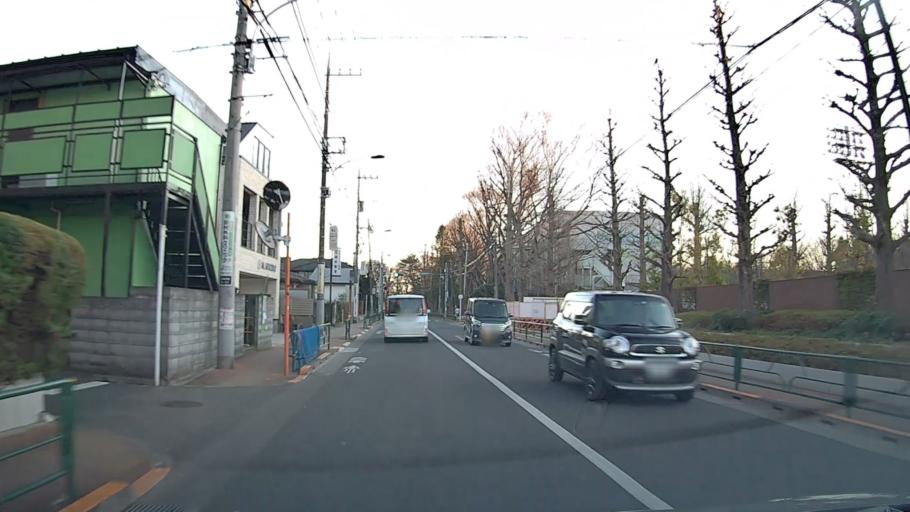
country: JP
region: Tokyo
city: Musashino
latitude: 35.7406
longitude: 139.5973
